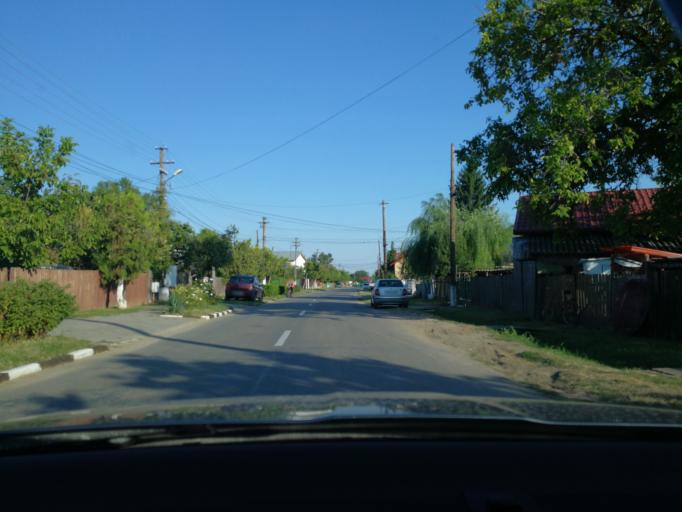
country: RO
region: Prahova
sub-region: Comuna Ceptura
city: Ceptura de Jos
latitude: 45.0152
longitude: 26.3309
